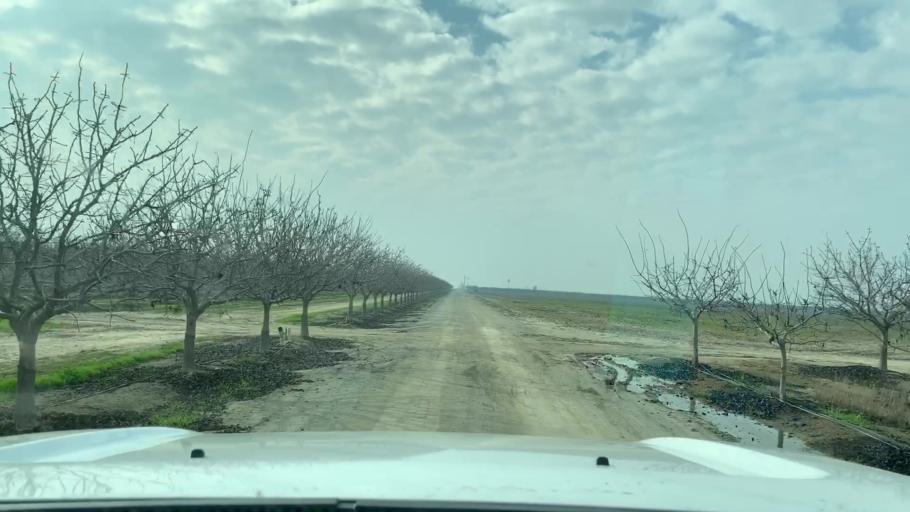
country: US
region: California
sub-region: Tulare County
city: Earlimart
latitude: 35.8337
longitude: -119.3617
